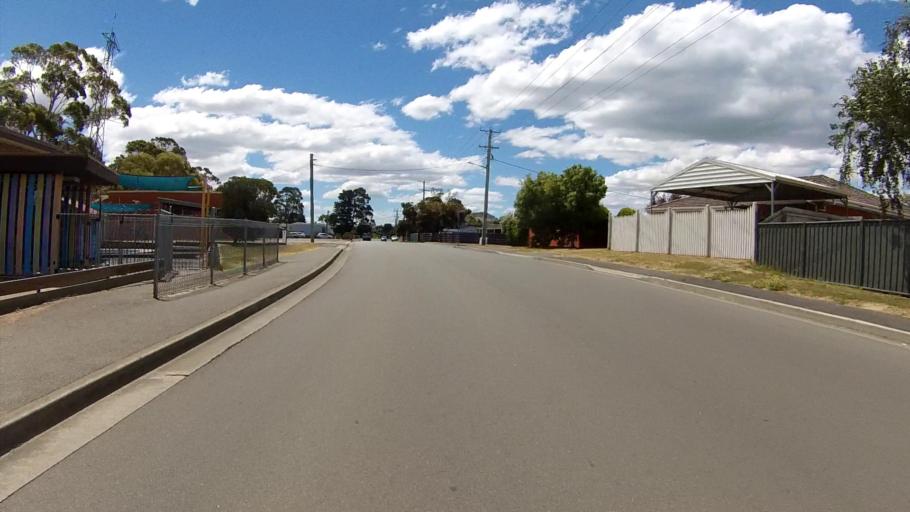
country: AU
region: Tasmania
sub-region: Clarence
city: Lauderdale
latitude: -42.9100
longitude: 147.4924
